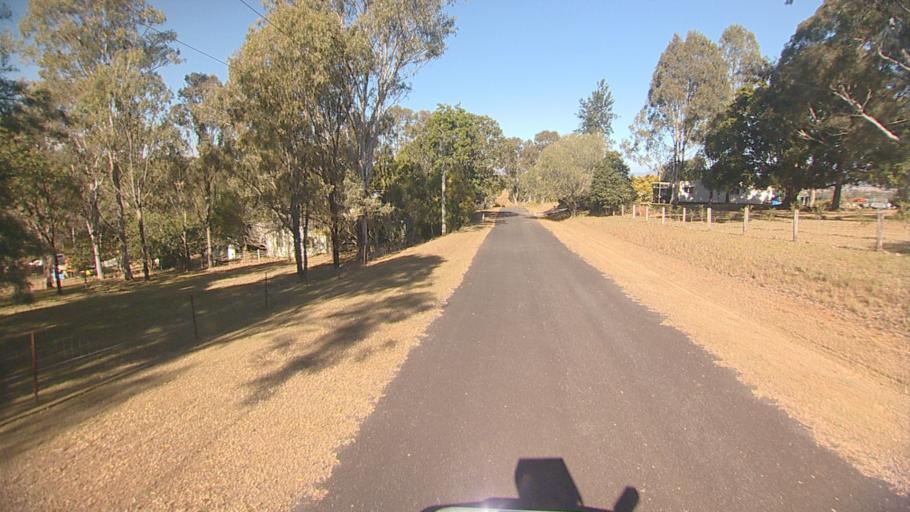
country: AU
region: Queensland
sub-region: Logan
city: Cedar Vale
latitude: -27.8931
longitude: 152.9789
